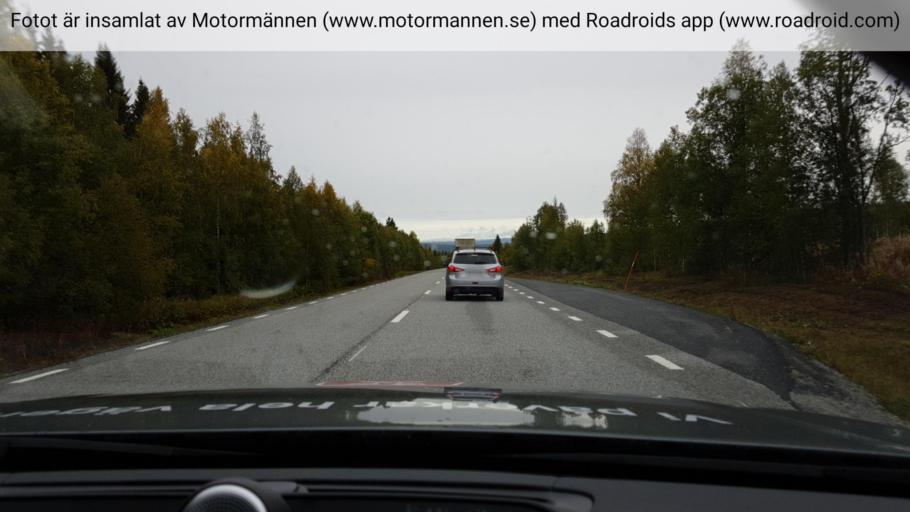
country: SE
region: Jaemtland
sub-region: Stroemsunds Kommun
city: Stroemsund
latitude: 64.1155
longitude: 15.6178
